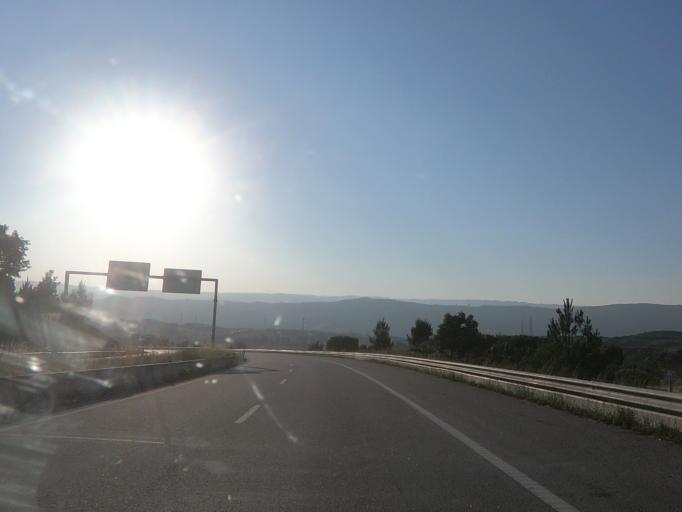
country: PT
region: Guarda
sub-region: Celorico da Beira
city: Celorico da Beira
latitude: 40.6277
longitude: -7.4062
